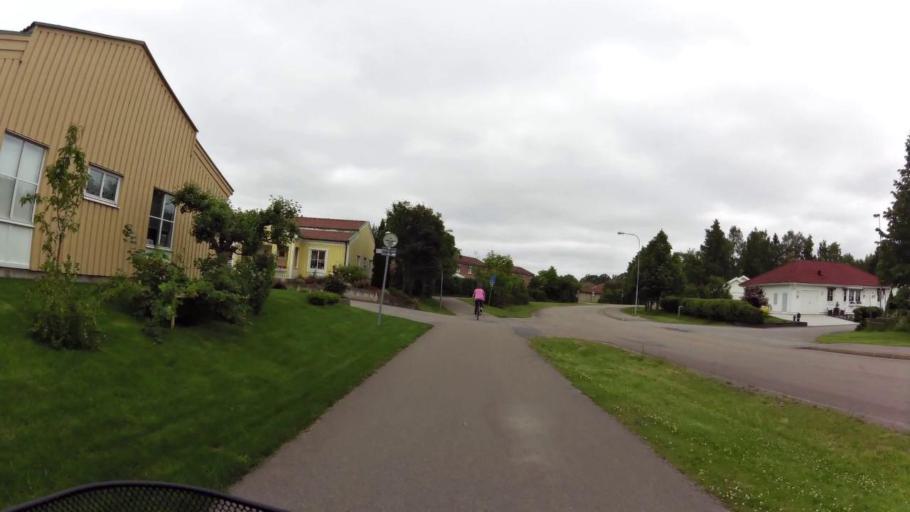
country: SE
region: OEstergoetland
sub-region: Linkopings Kommun
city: Sturefors
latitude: 58.3699
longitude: 15.6873
